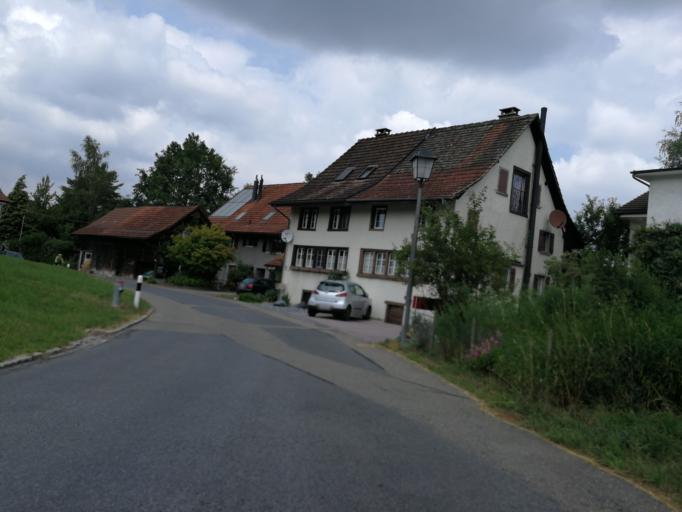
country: CH
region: Zurich
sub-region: Bezirk Hinwil
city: Gruet
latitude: 47.2921
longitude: 8.7778
